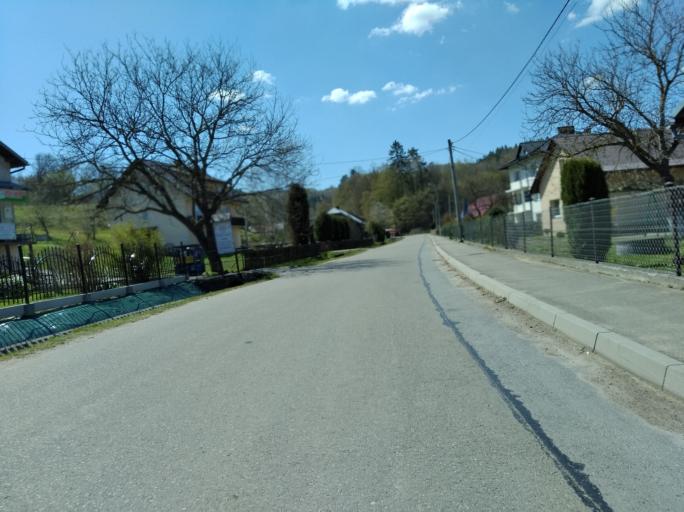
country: PL
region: Subcarpathian Voivodeship
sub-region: Powiat brzozowski
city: Dydnia
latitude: 49.6907
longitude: 22.2167
